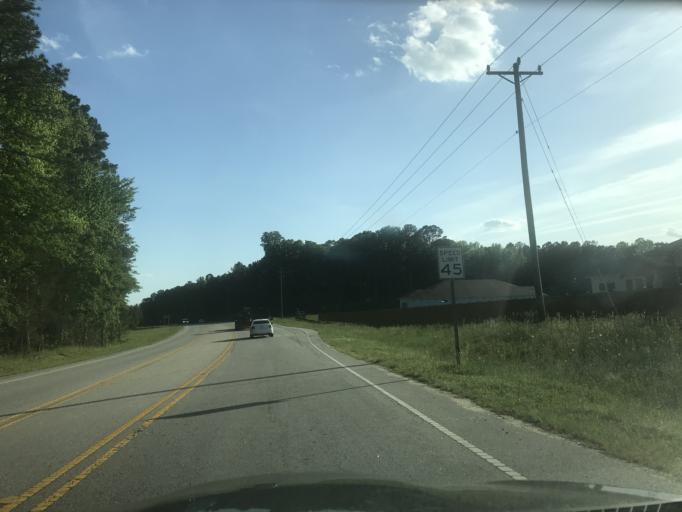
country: US
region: North Carolina
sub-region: Wake County
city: Wendell
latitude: 35.7593
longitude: -78.4247
